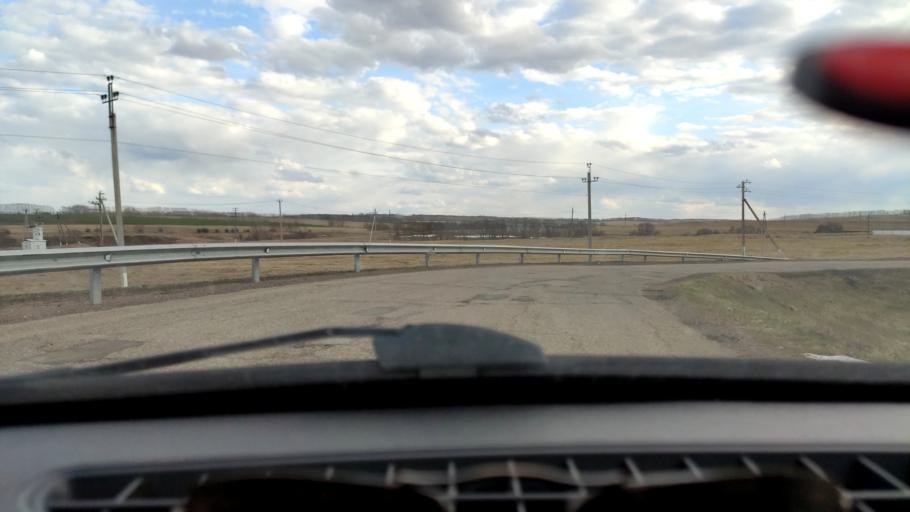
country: RU
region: Bashkortostan
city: Karmaskaly
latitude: 54.3818
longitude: 56.2193
